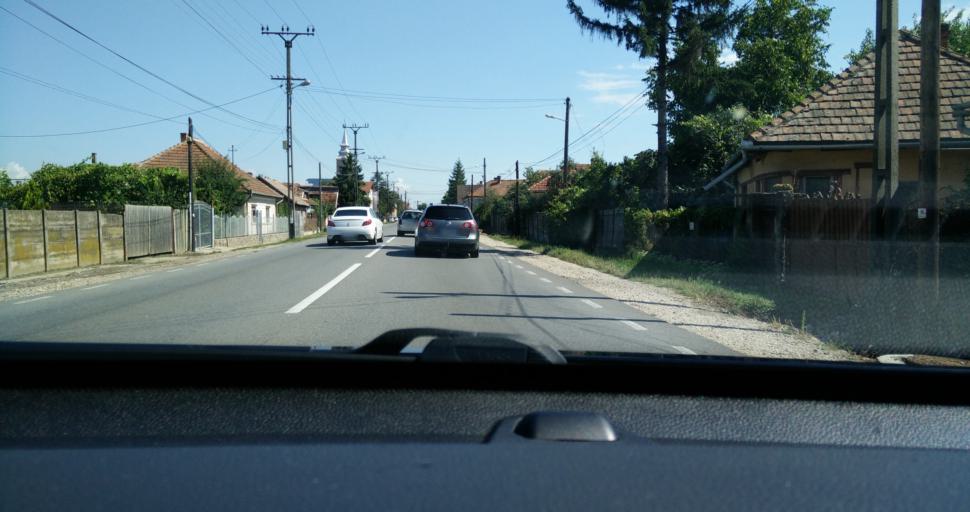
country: RO
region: Bihor
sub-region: Comuna Osorheiu
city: Alparea
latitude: 47.0427
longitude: 22.0327
